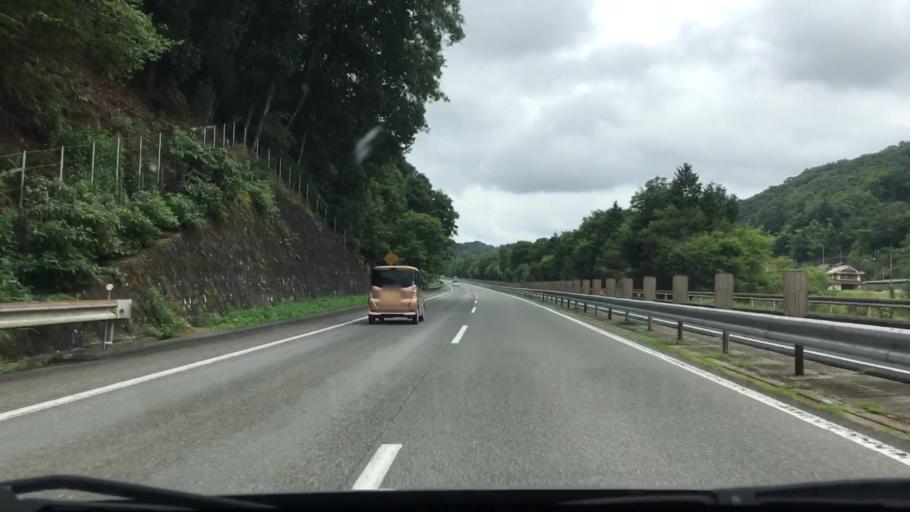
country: JP
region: Hiroshima
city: Miyoshi
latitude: 34.7653
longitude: 132.7939
